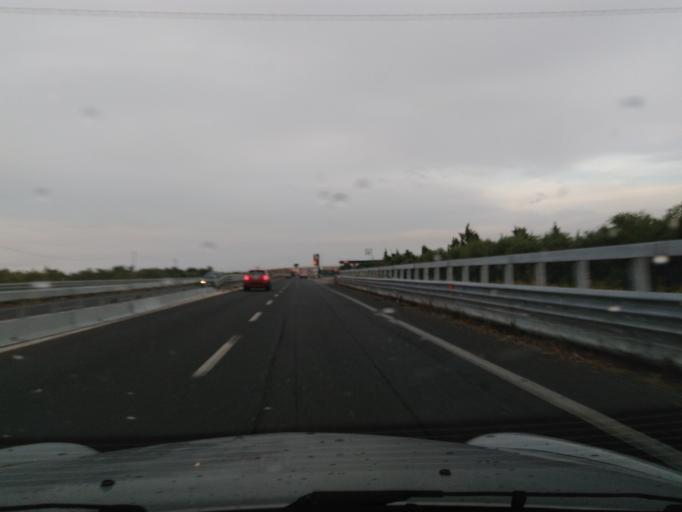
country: IT
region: Apulia
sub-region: Provincia di Bari
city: Giovinazzo
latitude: 41.1736
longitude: 16.6825
